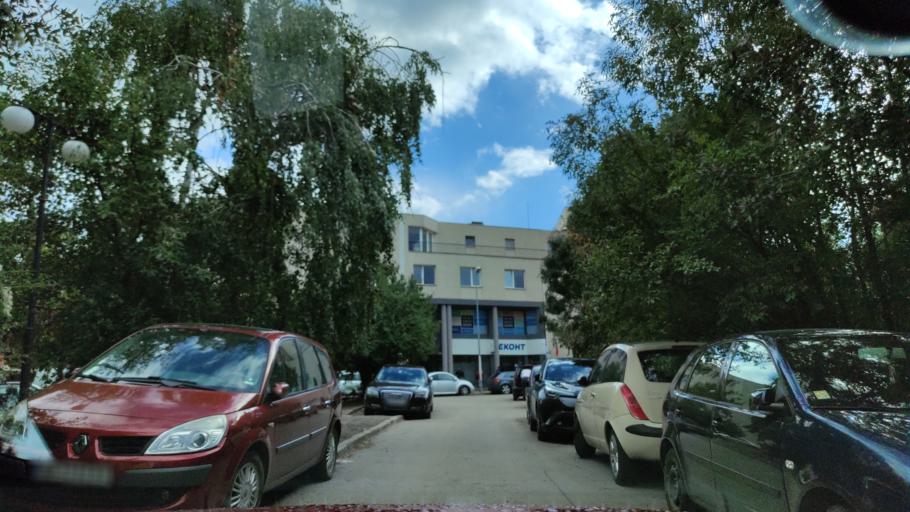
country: BG
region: Sofia-Capital
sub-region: Stolichna Obshtina
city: Sofia
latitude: 42.6539
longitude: 23.3423
